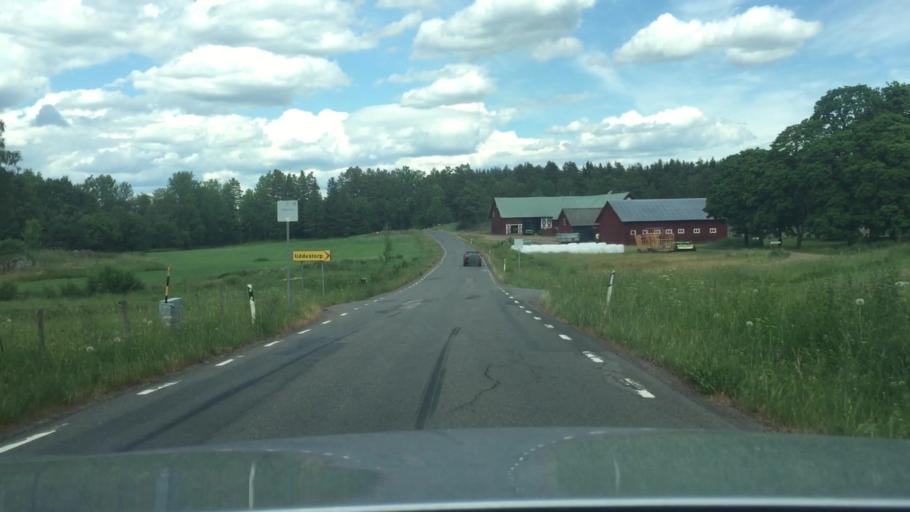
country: SE
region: Vaestra Goetaland
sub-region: Tidaholms Kommun
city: Tidaholm
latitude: 58.2073
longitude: 13.9829
